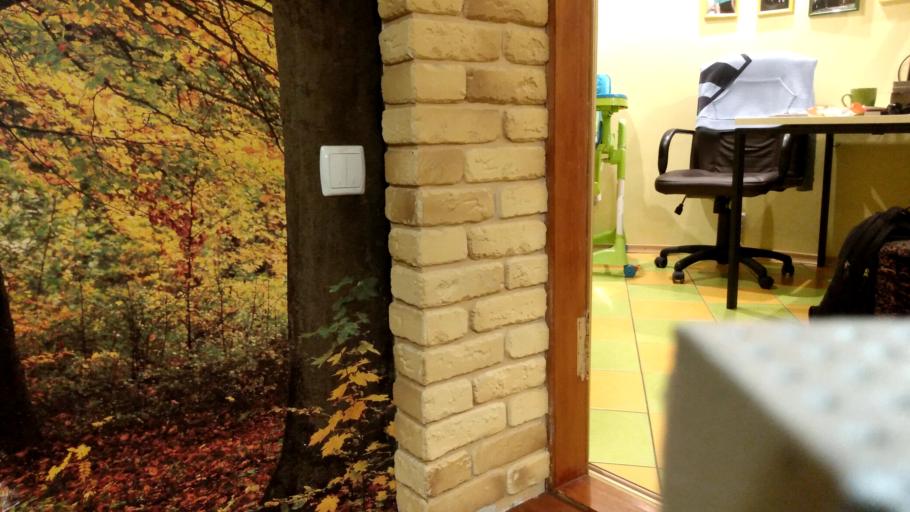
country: RU
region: Republic of Karelia
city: Pudozh
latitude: 61.7709
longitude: 37.6823
